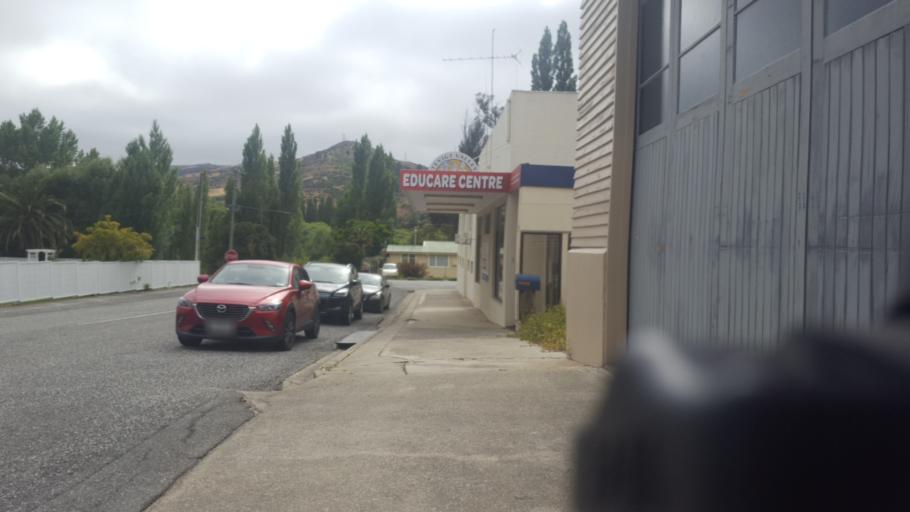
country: NZ
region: Otago
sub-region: Queenstown-Lakes District
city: Kingston
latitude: -45.5406
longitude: 169.3157
